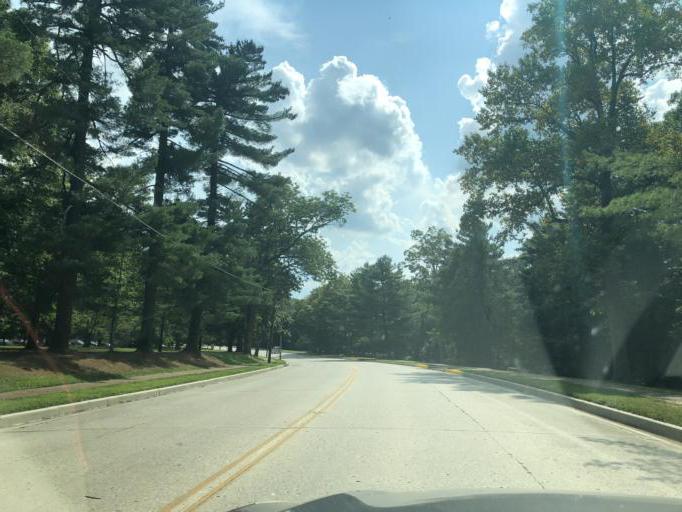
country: US
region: Tennessee
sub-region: Franklin County
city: Sewanee
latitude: 35.2069
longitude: -85.9197
